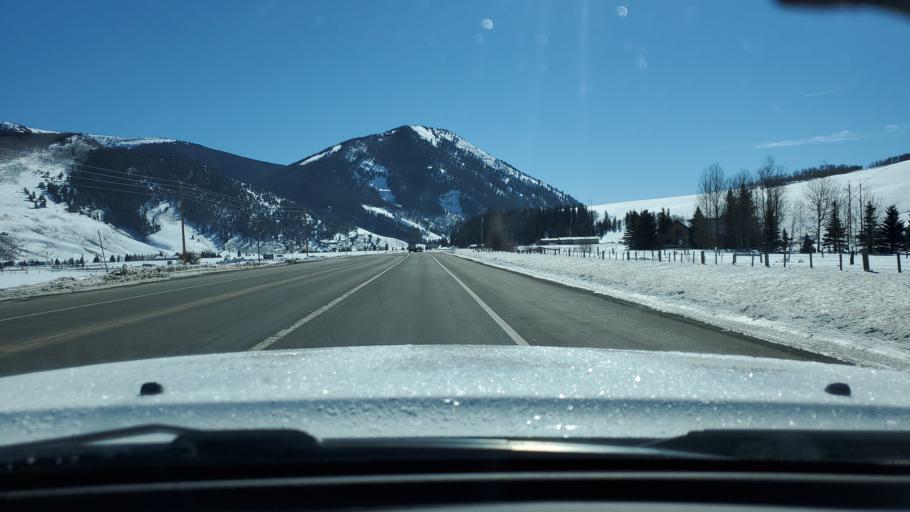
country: US
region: Colorado
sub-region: Gunnison County
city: Crested Butte
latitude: 38.8052
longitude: -106.8918
